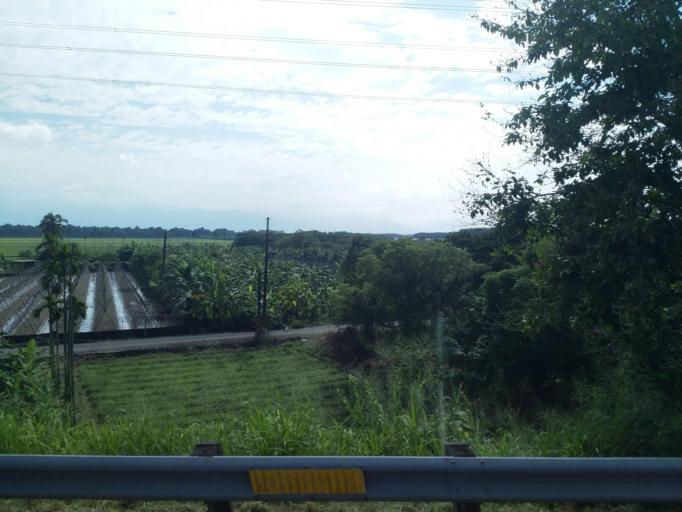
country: TW
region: Taiwan
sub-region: Pingtung
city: Pingtung
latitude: 22.8349
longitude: 120.4937
